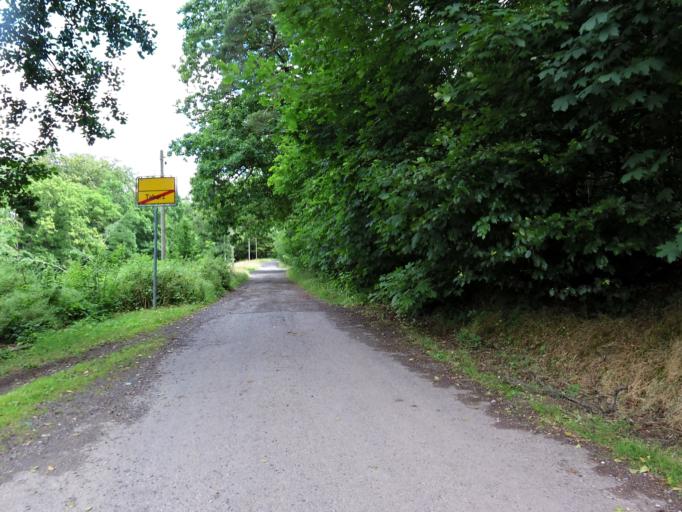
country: DE
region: Thuringia
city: Tabarz
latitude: 50.8691
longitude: 10.5235
